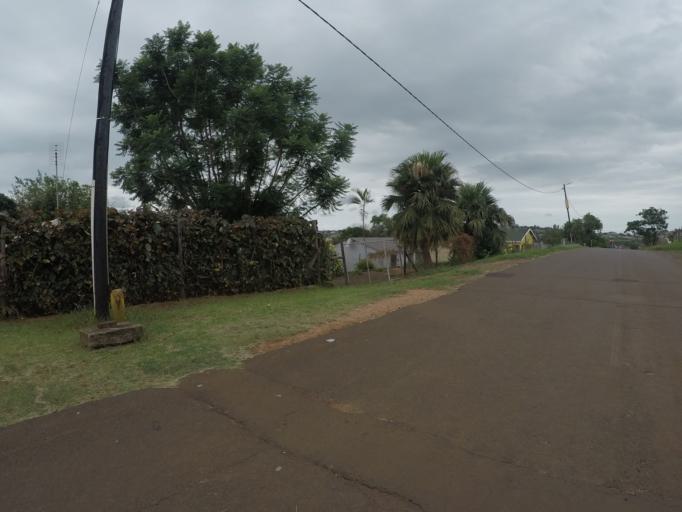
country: ZA
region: KwaZulu-Natal
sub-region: uThungulu District Municipality
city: Empangeni
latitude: -28.7739
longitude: 31.8581
